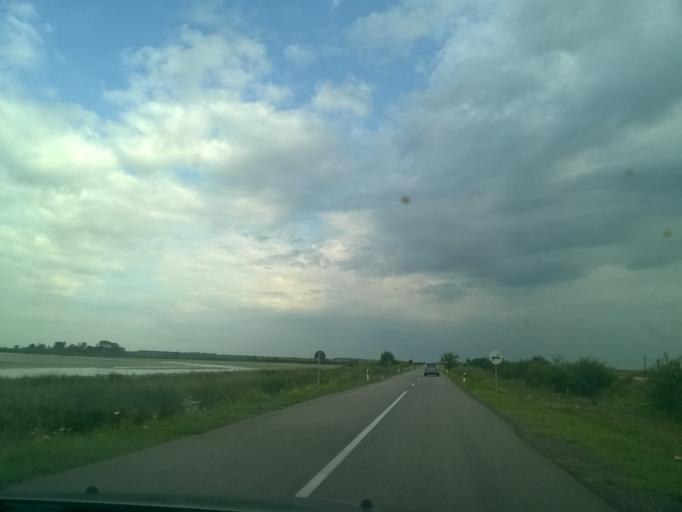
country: RS
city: Uzdin
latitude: 45.2186
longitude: 20.6306
